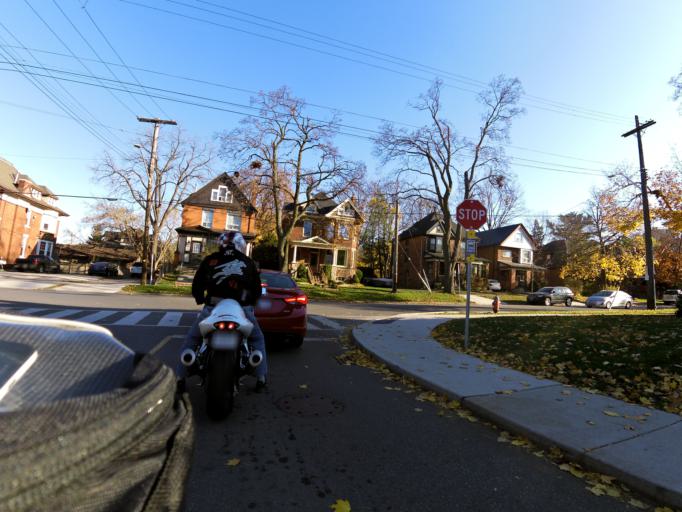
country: CA
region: Ontario
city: Hamilton
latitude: 43.2458
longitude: -79.8410
